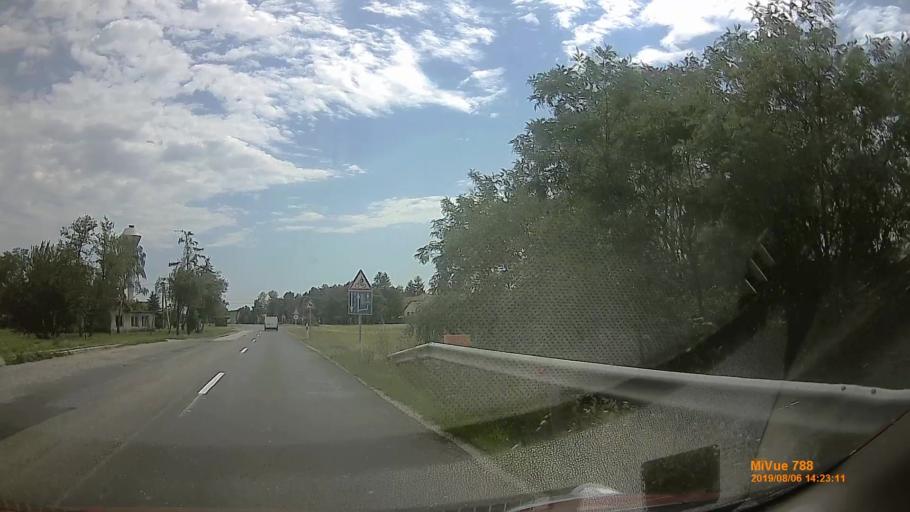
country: HU
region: Vas
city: Vasvar
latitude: 47.1564
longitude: 16.8033
